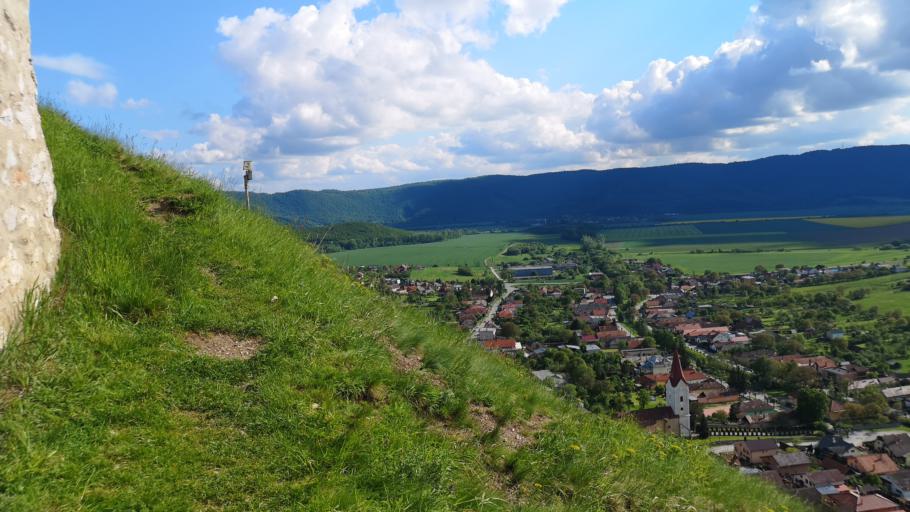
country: SK
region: Kosicky
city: Roznava
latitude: 48.6586
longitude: 20.5997
